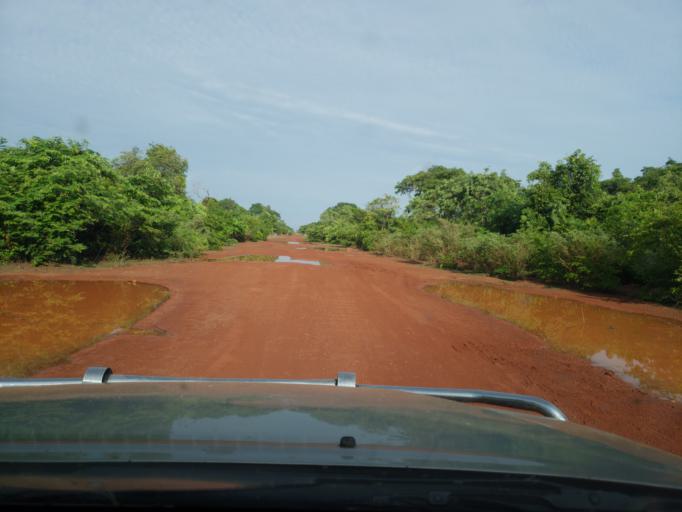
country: ML
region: Sikasso
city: Koutiala
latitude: 12.4169
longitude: -5.7145
